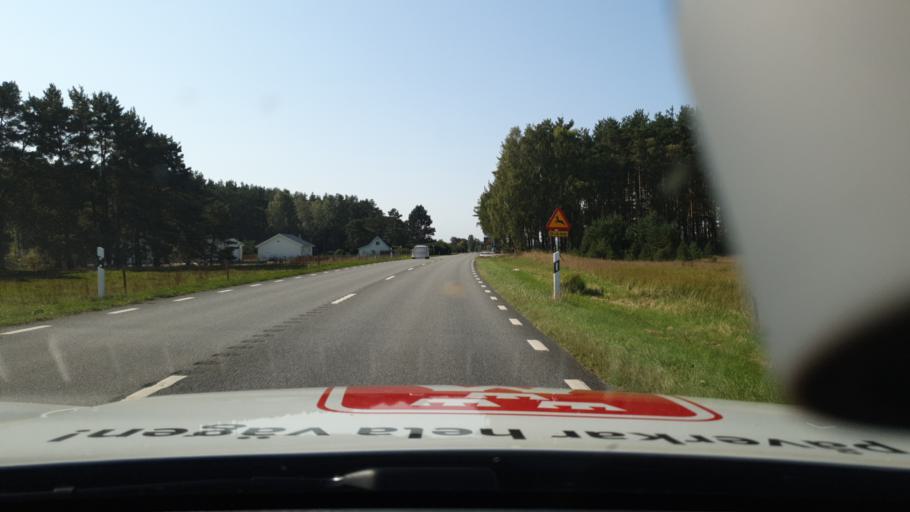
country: SE
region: Skane
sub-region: Kristianstads Kommun
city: Ahus
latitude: 55.8908
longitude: 14.2436
